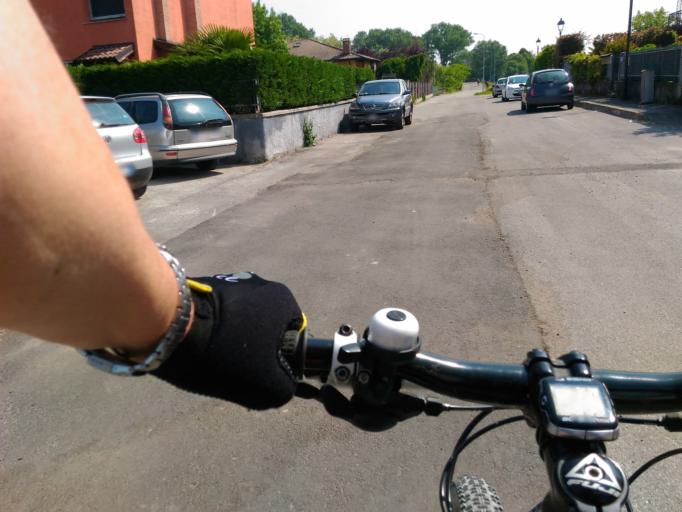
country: IT
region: Lombardy
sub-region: Provincia di Lodi
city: Castiraga Vidardo
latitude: 45.2573
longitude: 9.4089
